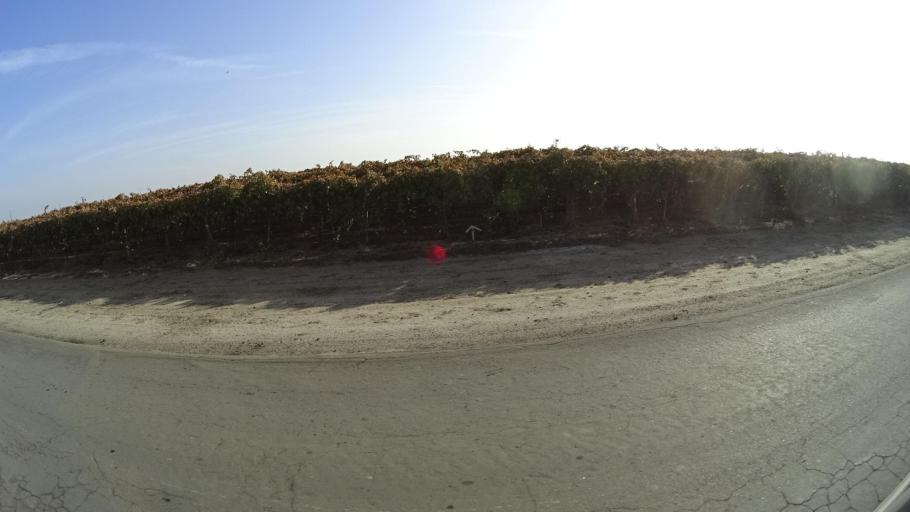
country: US
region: California
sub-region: Kern County
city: McFarland
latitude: 35.6994
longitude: -119.1871
